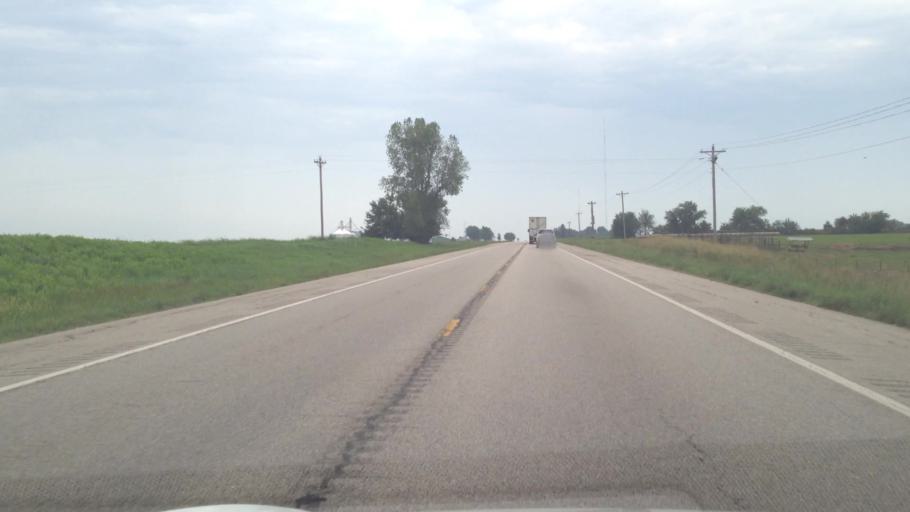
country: US
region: Missouri
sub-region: Jasper County
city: Carl Junction
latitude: 37.2454
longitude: -94.7051
